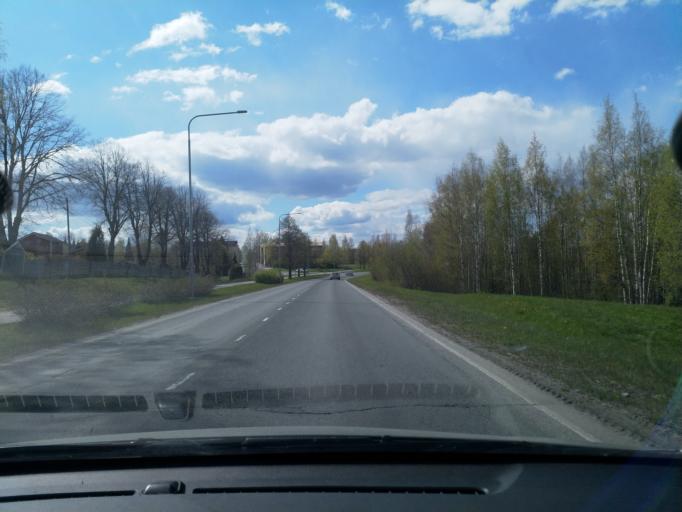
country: FI
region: Pirkanmaa
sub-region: Tampere
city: Tampere
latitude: 61.4801
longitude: 23.8149
